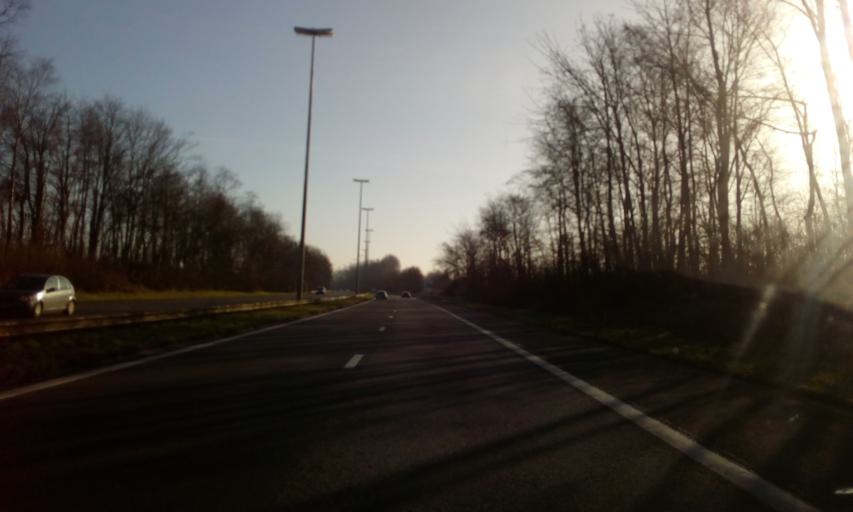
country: BE
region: Wallonia
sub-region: Province du Hainaut
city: Pont-a-Celles
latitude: 50.5301
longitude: 4.3821
